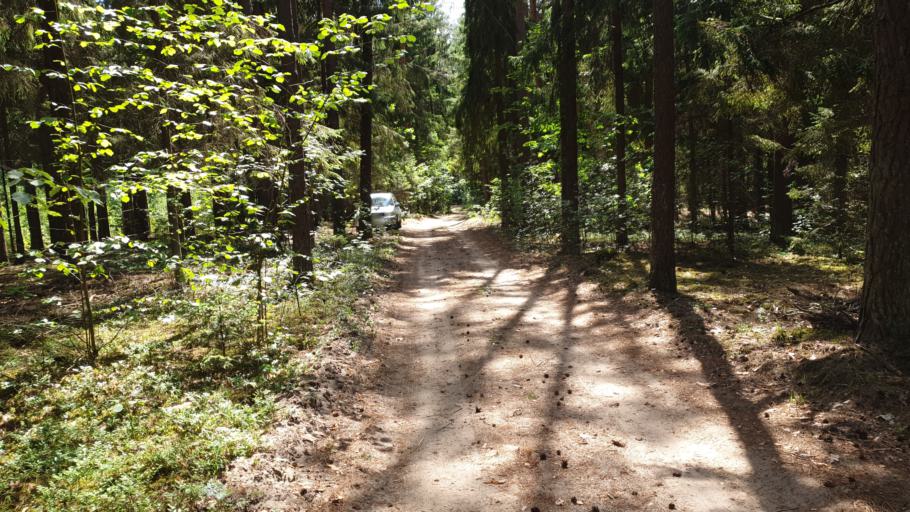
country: LT
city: Grigiskes
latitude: 54.7767
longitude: 24.9928
